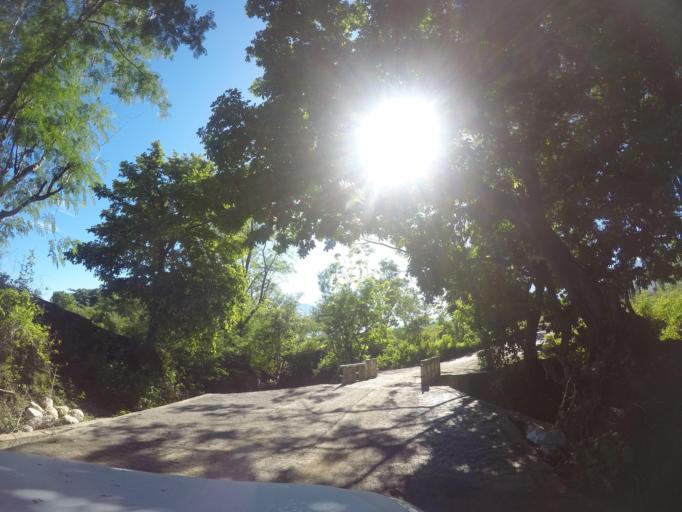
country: TL
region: Bobonaro
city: Maliana
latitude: -8.9976
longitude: 125.1920
